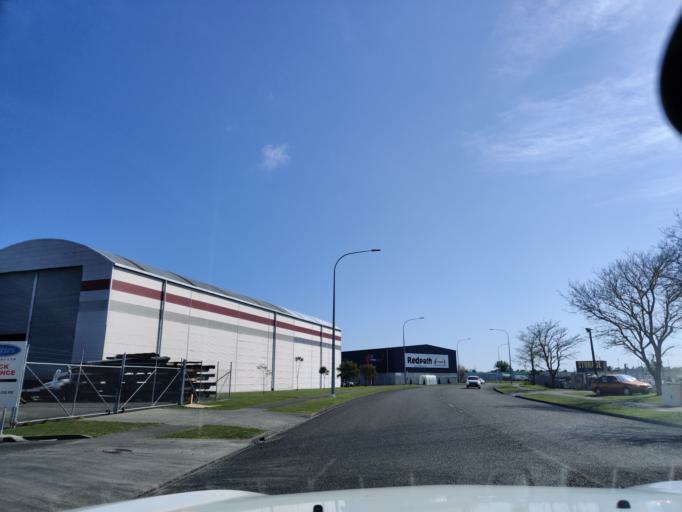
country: NZ
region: Manawatu-Wanganui
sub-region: Palmerston North City
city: Palmerston North
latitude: -40.3353
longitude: 175.6445
